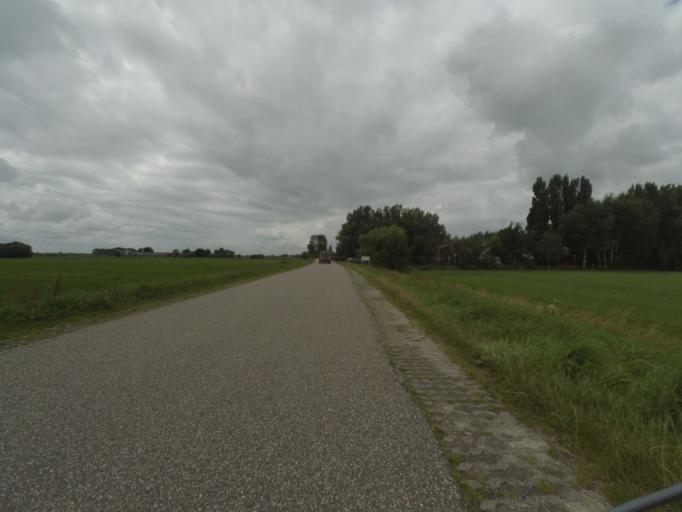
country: NL
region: Friesland
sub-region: Gemeente Dongeradeel
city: Anjum
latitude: 53.3205
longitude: 6.0995
